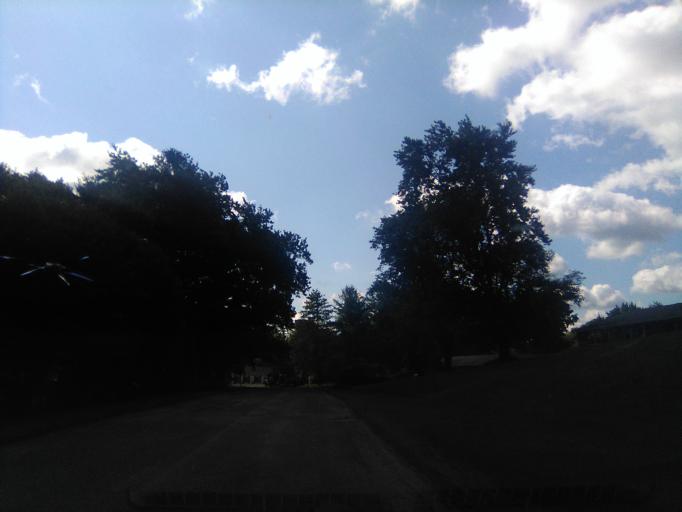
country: US
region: Tennessee
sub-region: Davidson County
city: Belle Meade
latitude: 36.1078
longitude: -86.8696
